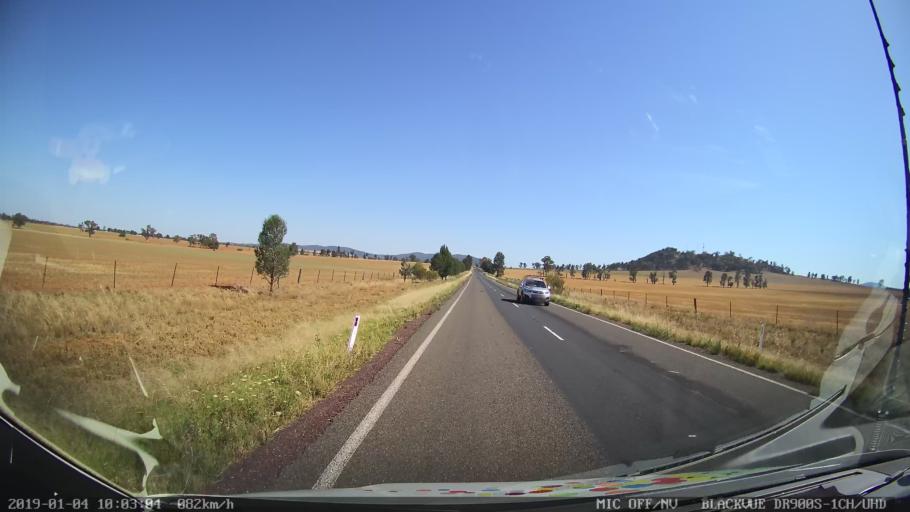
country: AU
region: New South Wales
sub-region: Cabonne
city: Canowindra
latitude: -33.4684
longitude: 148.3648
